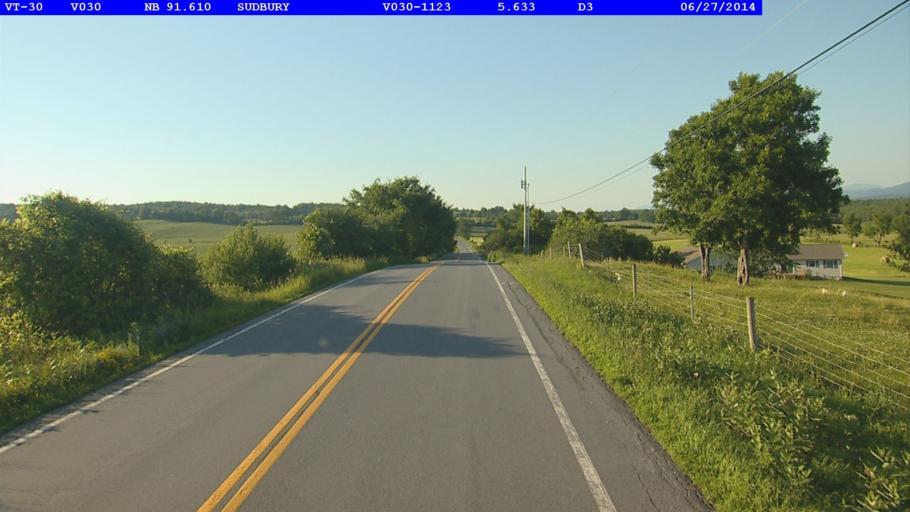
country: US
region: Vermont
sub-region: Rutland County
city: Brandon
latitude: 43.8274
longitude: -73.1934
